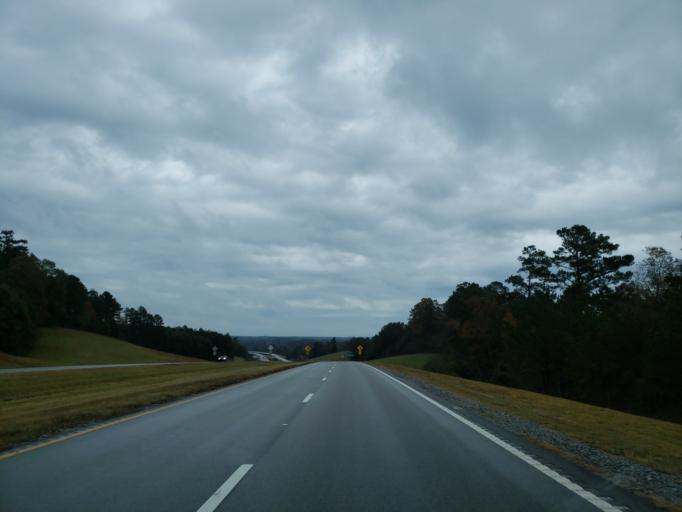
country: US
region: Mississippi
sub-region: Wayne County
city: Waynesboro
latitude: 31.6829
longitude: -88.6923
